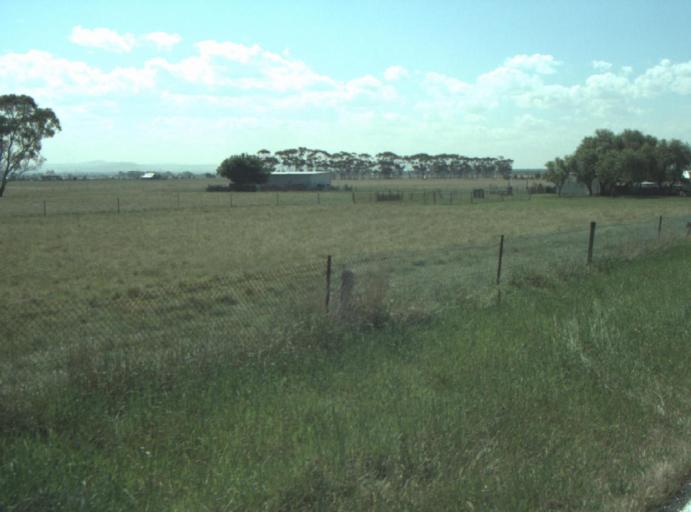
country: AU
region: Victoria
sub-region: Greater Geelong
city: Lara
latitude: -37.9983
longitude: 144.4007
